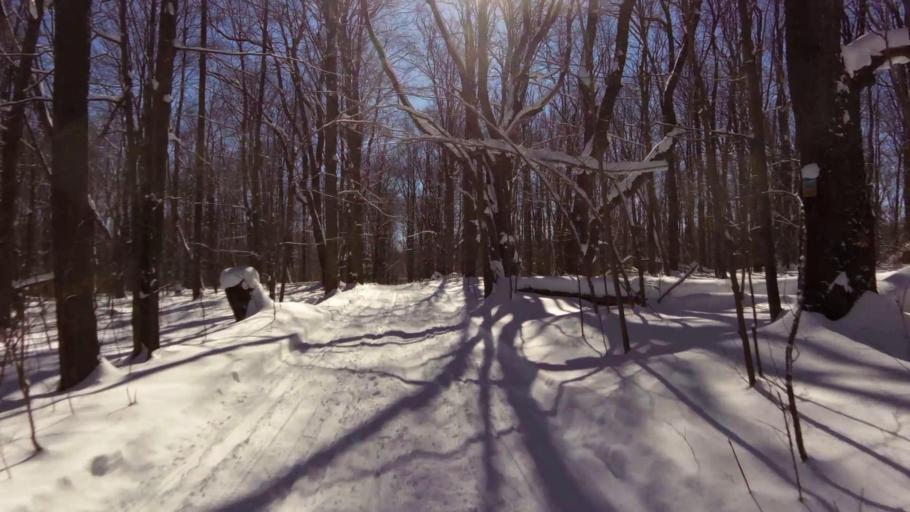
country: US
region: New York
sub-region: Chautauqua County
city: Mayville
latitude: 42.2139
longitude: -79.5348
